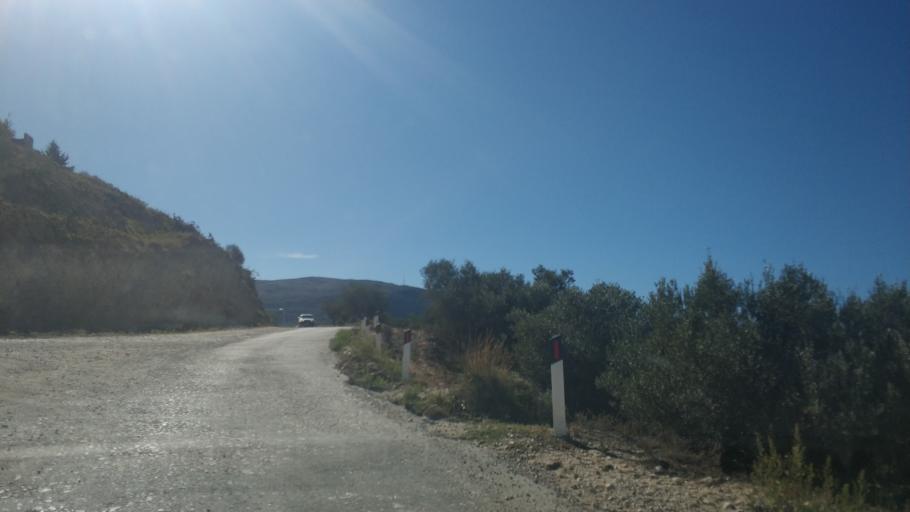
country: AL
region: Vlore
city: Vlore
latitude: 40.4499
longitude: 19.5158
